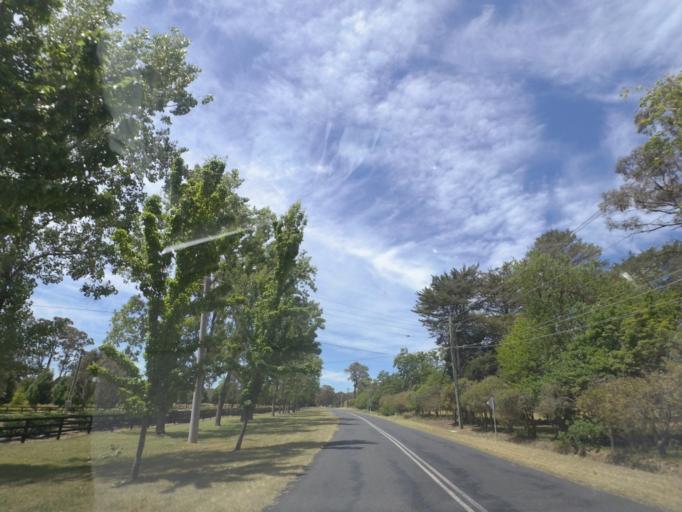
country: AU
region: New South Wales
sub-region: Wingecarribee
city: Colo Vale
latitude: -34.4095
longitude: 150.5240
